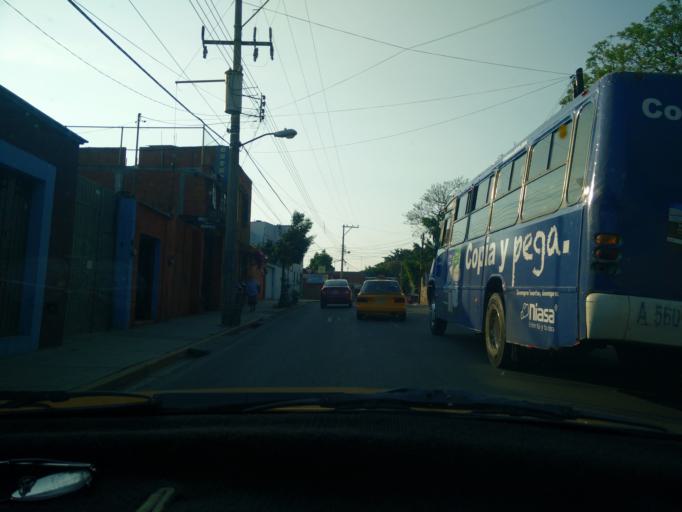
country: MX
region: Oaxaca
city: Oaxaca de Juarez
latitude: 17.0754
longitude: -96.7393
